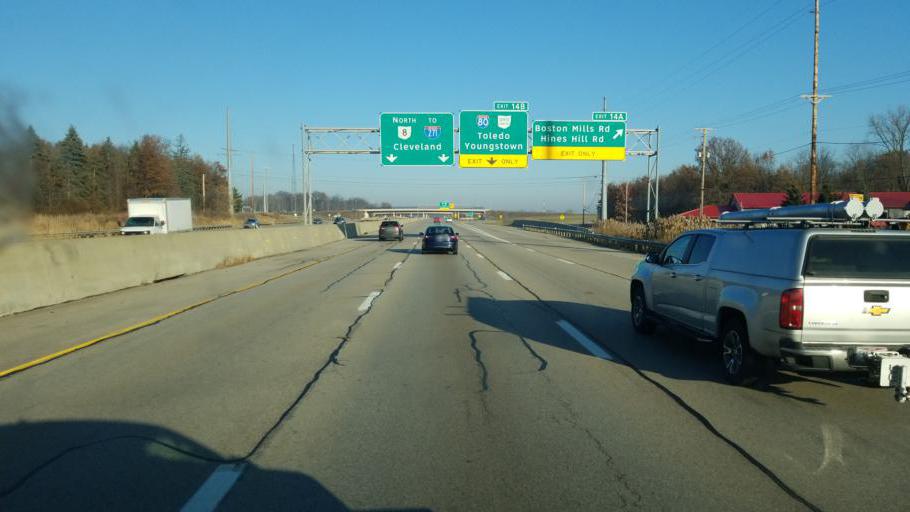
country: US
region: Ohio
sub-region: Summit County
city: Boston Heights
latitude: 41.2496
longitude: -81.4982
